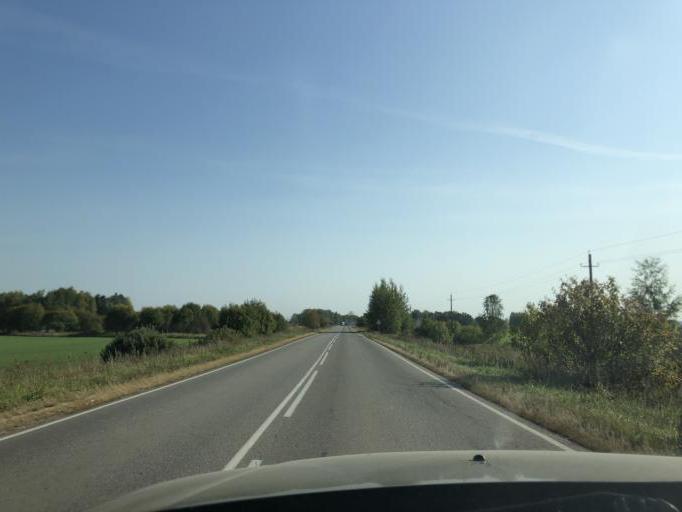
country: RU
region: Tula
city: Novogurovskiy
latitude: 54.4505
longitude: 37.4278
